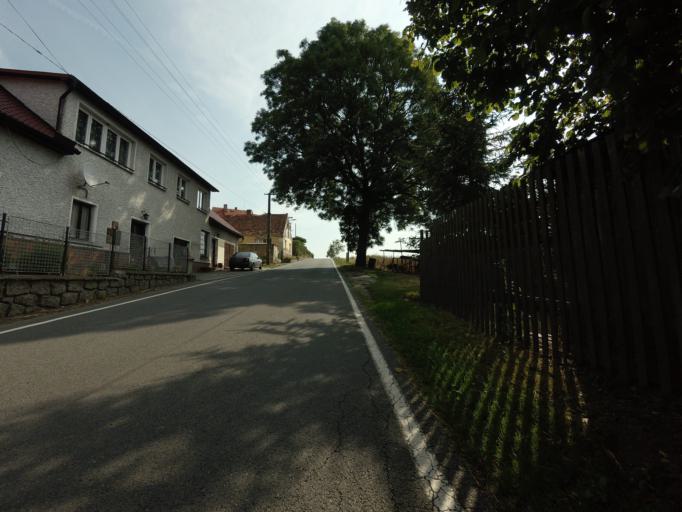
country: CZ
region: Central Bohemia
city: Petrovice
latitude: 49.5553
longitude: 14.3422
